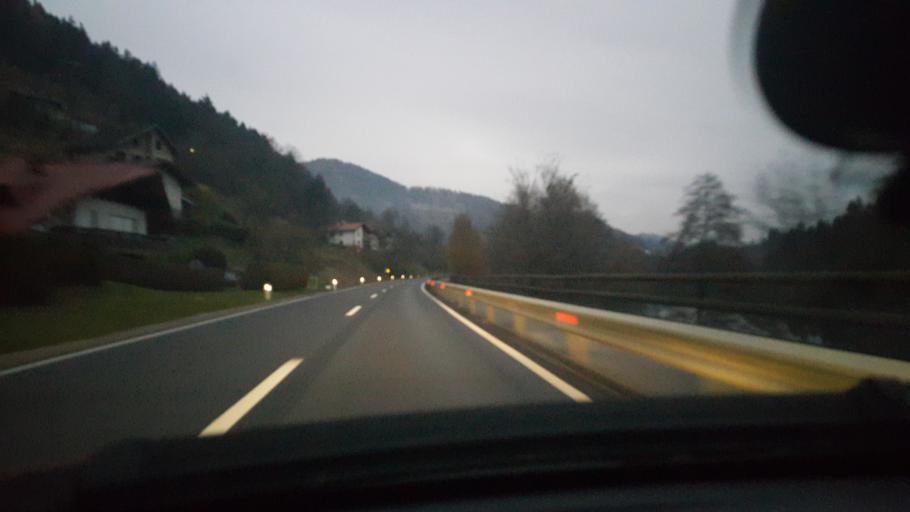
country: SI
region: Dravograd
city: Dravograd
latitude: 46.5949
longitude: 15.0068
